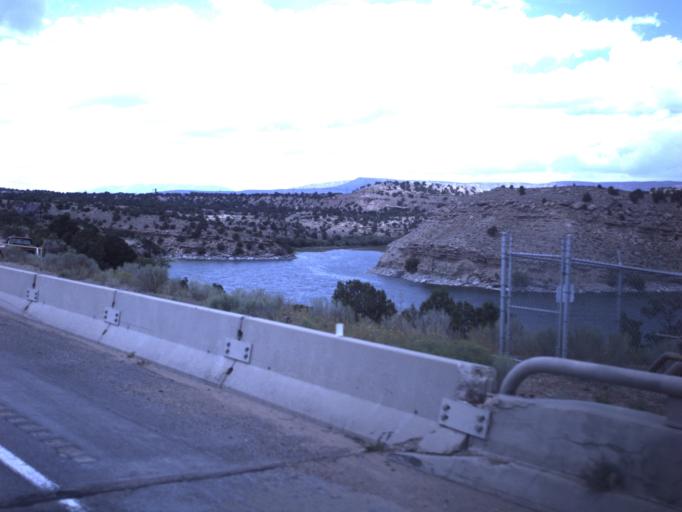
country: US
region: Utah
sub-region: Duchesne County
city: Duchesne
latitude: 40.1739
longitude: -110.4993
